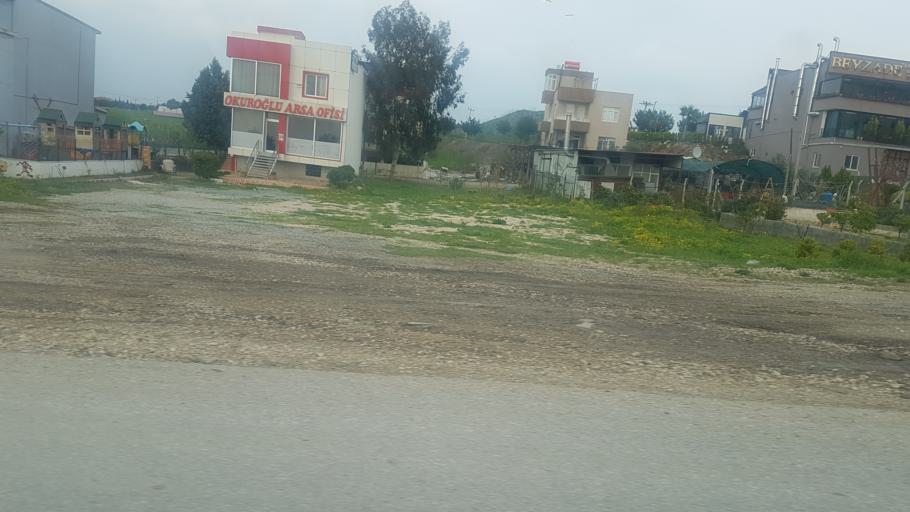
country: TR
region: Adana
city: Seyhan
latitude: 37.0576
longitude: 35.2436
